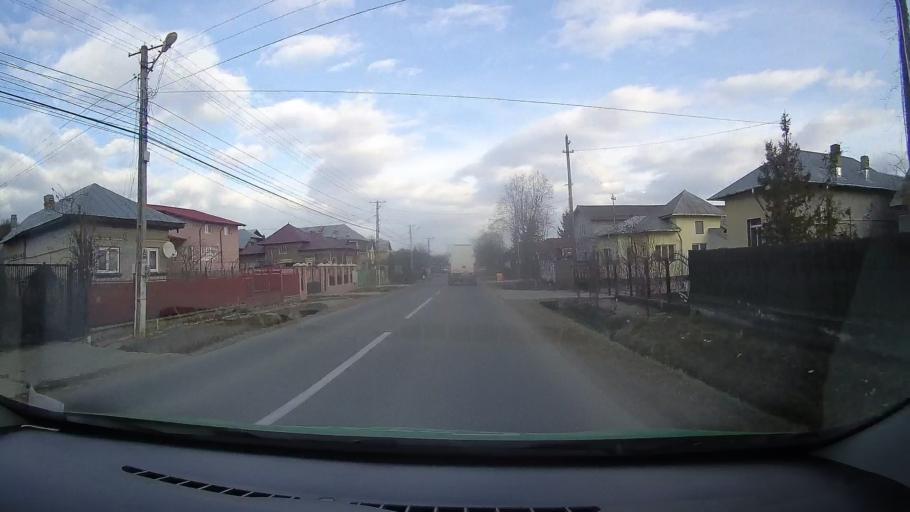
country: RO
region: Dambovita
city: Razvad
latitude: 44.9319
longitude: 25.5479
